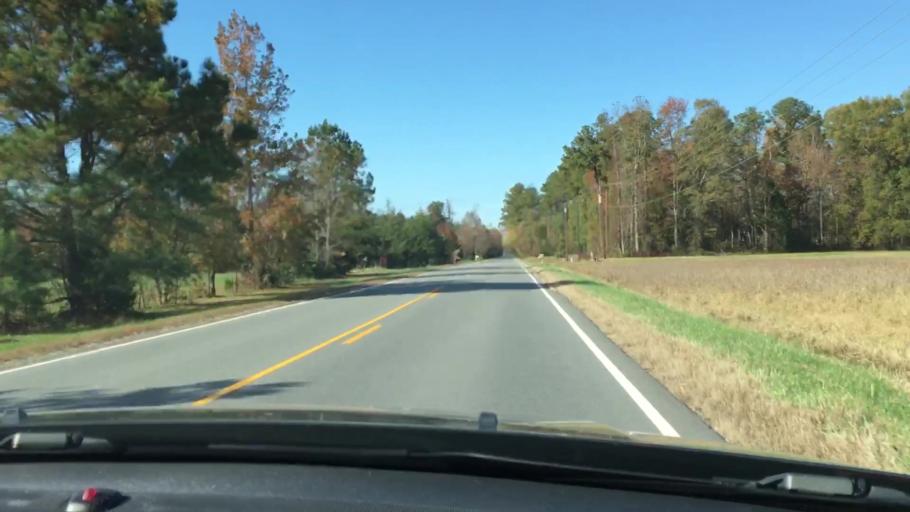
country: US
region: Virginia
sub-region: King William County
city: King William
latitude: 37.6631
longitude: -76.9623
